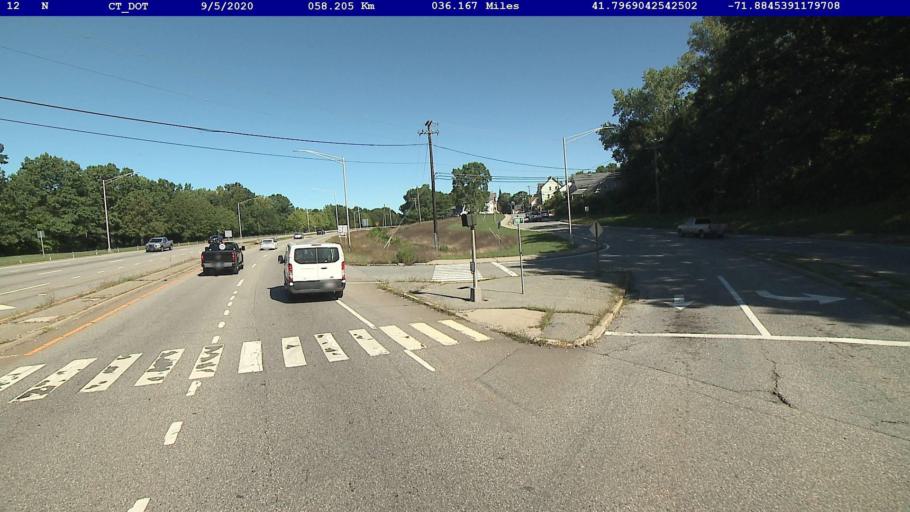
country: US
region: Connecticut
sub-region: Windham County
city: Danielson
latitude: 41.7969
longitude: -71.8845
